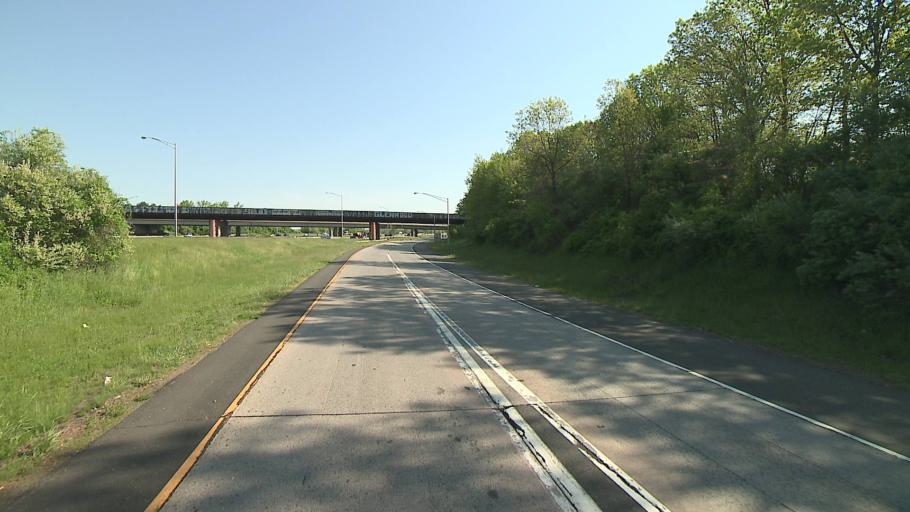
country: US
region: Connecticut
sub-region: Hartford County
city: Manchester
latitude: 41.7935
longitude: -72.5597
